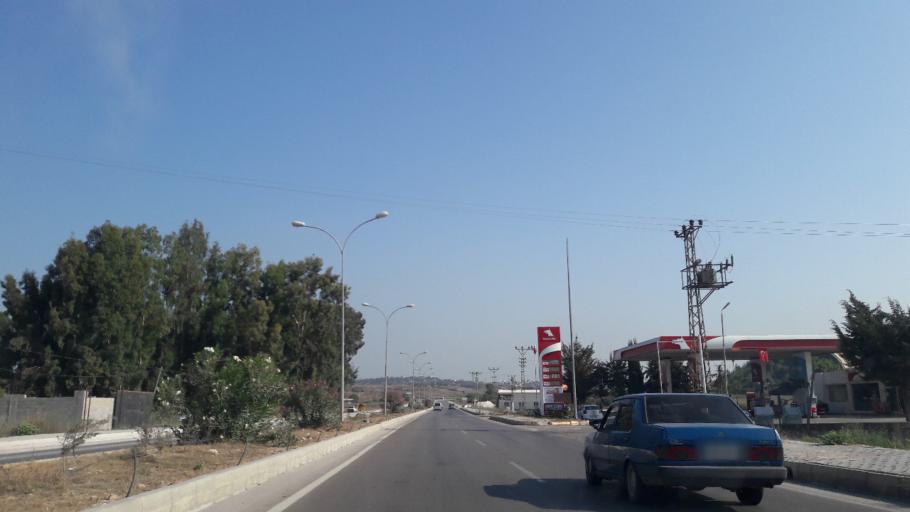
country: TR
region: Adana
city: Yuregir
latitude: 37.0550
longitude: 35.4414
